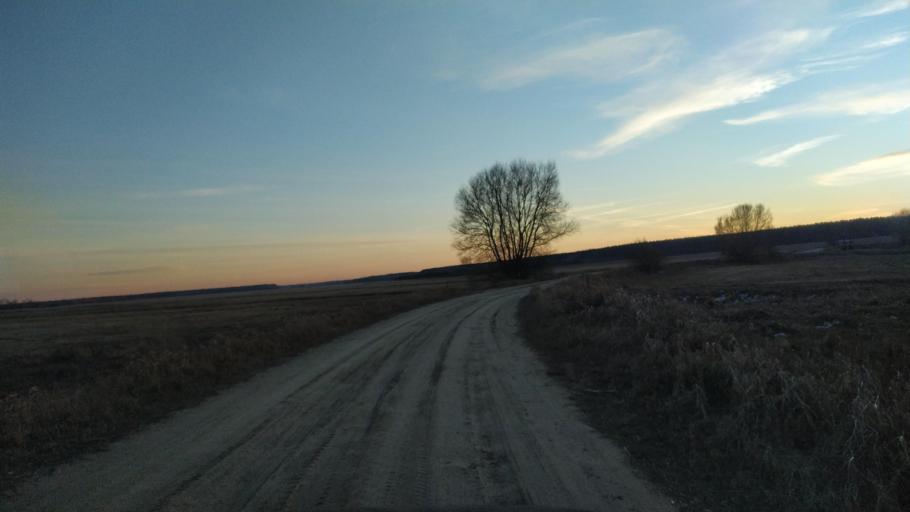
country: BY
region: Brest
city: Pruzhany
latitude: 52.5483
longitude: 24.2497
